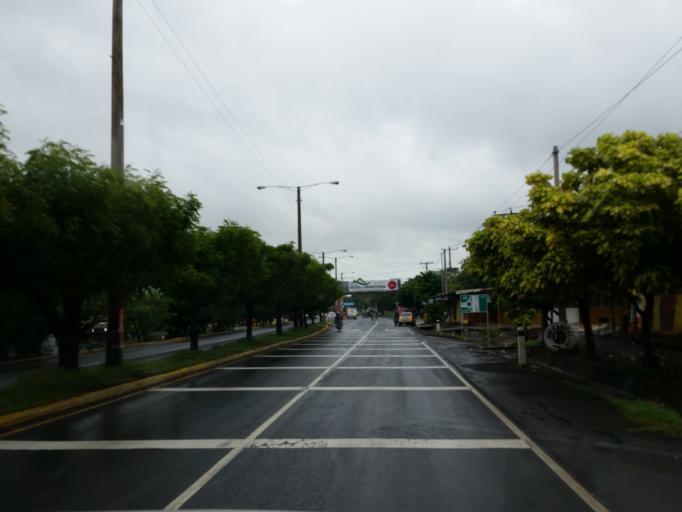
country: NI
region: Managua
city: Ciudad Sandino
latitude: 12.1675
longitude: -86.3420
